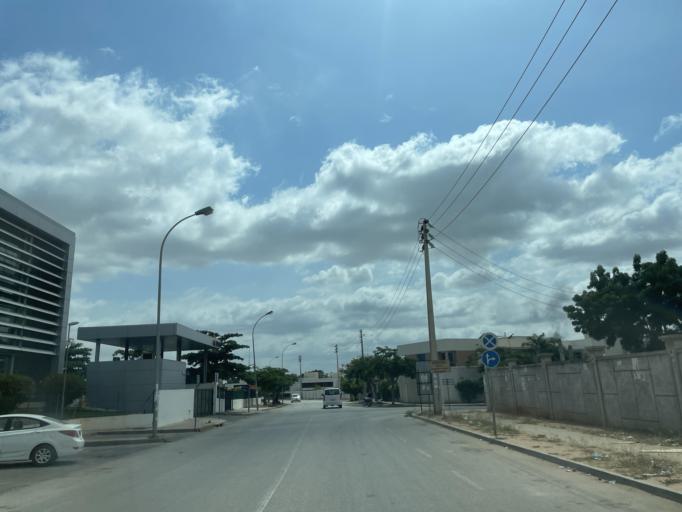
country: AO
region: Luanda
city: Luanda
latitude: -8.9310
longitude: 13.1886
